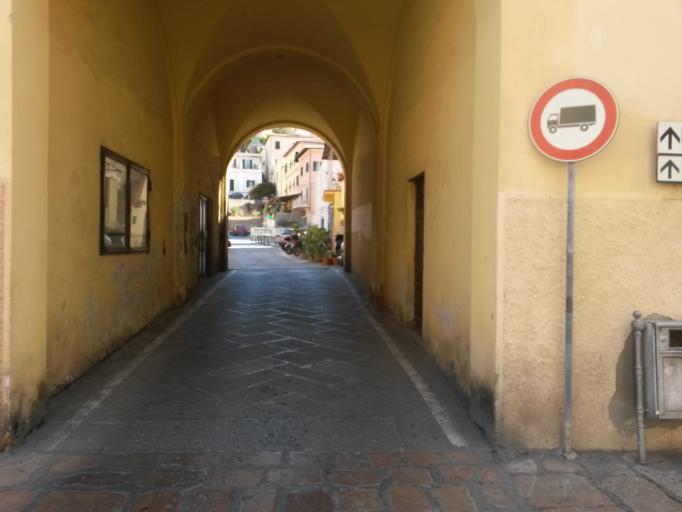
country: IT
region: Tuscany
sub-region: Provincia di Livorno
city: Portoferraio
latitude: 42.8143
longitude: 10.3318
